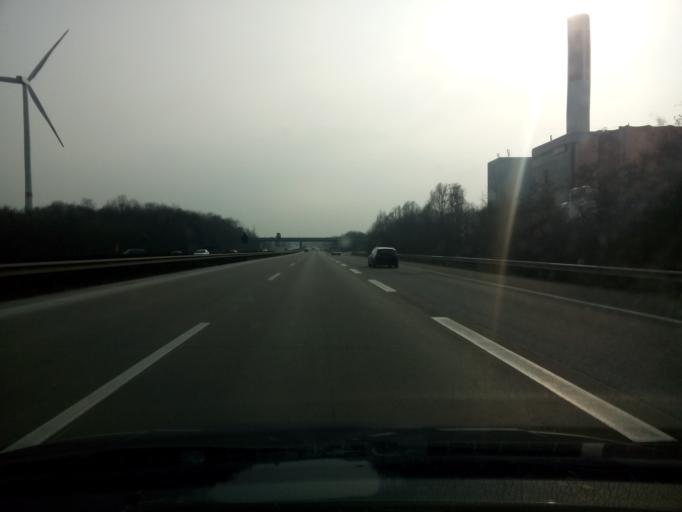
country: DE
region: Lower Saxony
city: Schiffdorf
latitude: 53.5497
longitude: 8.6194
